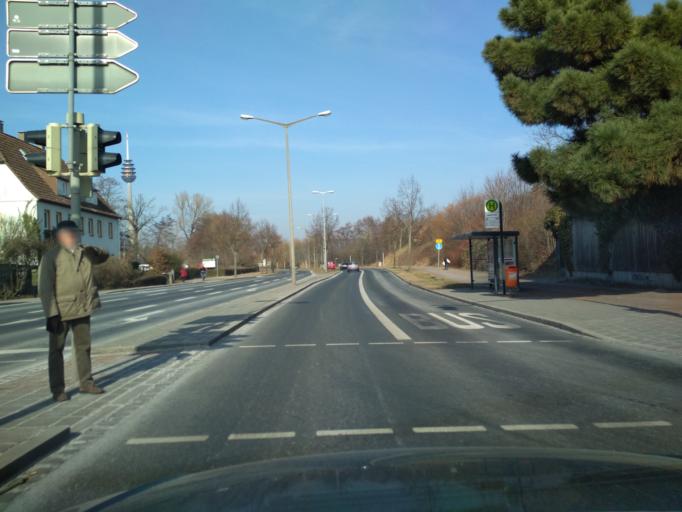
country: DE
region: Bavaria
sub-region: Regierungsbezirk Mittelfranken
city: Stein
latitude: 49.4138
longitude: 11.0348
